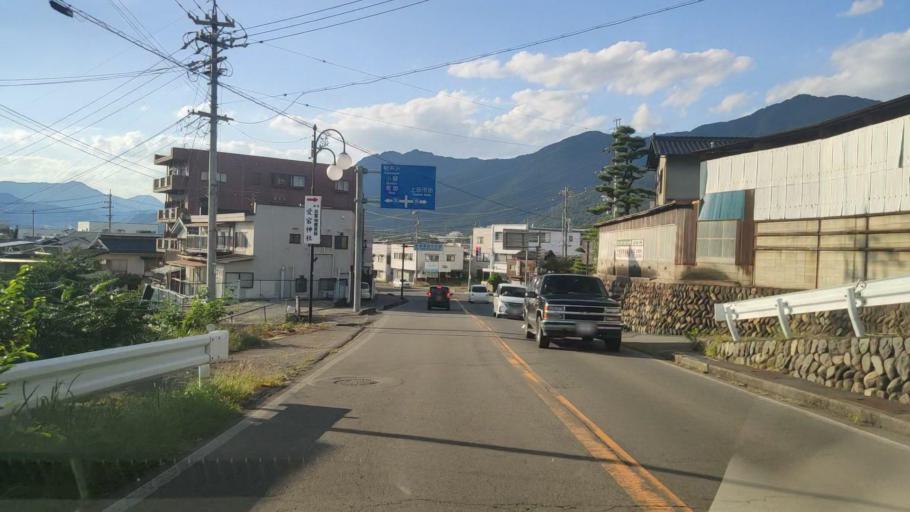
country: JP
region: Nagano
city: Ueda
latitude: 36.4040
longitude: 138.2625
